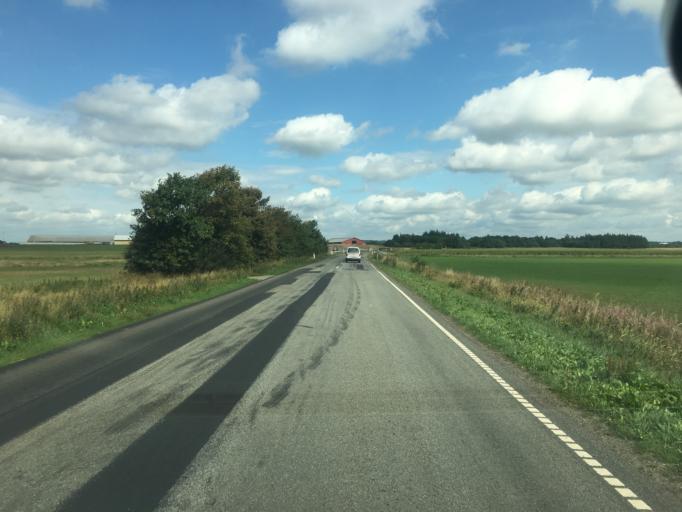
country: DK
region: South Denmark
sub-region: Tonder Kommune
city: Toftlund
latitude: 55.1094
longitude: 9.0331
